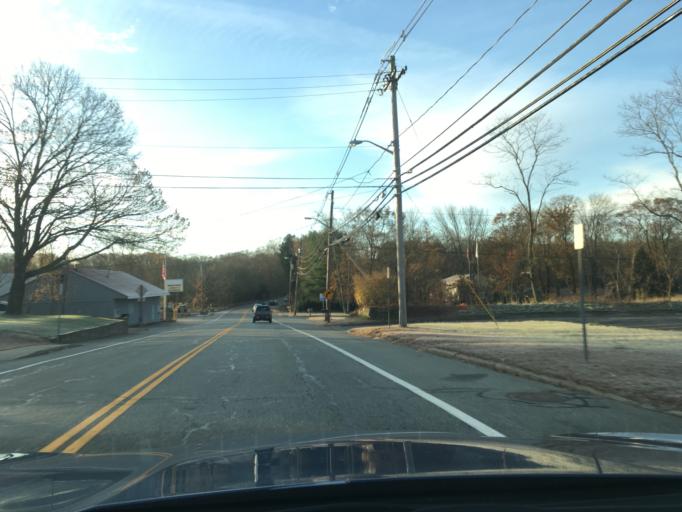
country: US
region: Rhode Island
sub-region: Washington County
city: North Kingstown
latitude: 41.5638
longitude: -71.4643
